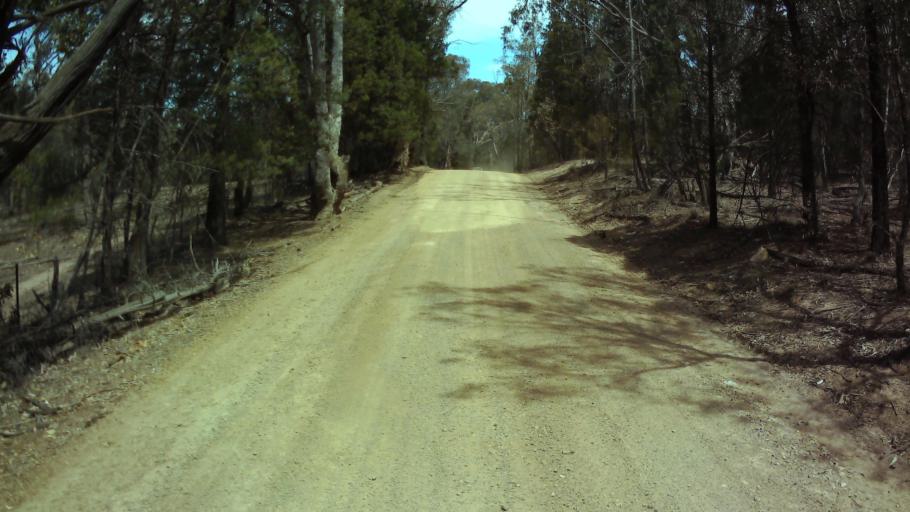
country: AU
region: New South Wales
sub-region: Weddin
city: Grenfell
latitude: -33.8178
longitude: 148.1661
